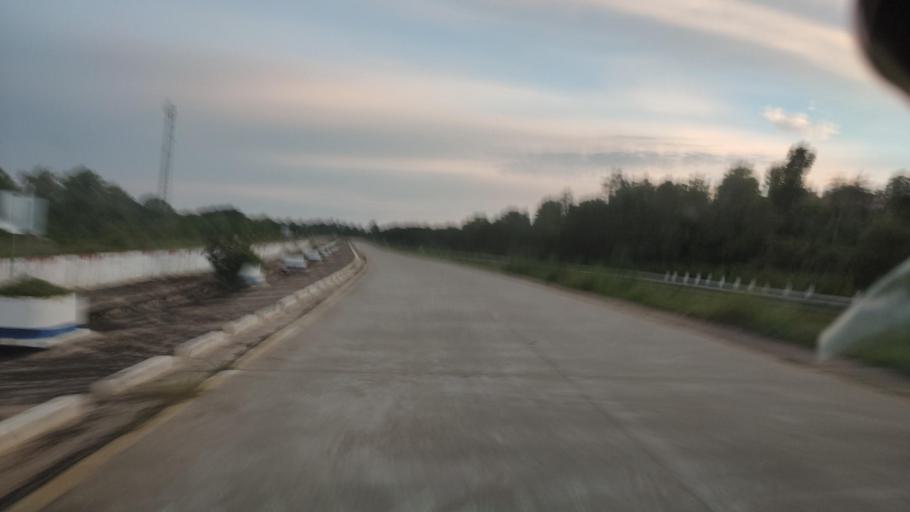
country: MM
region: Mandalay
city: Yamethin
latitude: 20.2221
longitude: 95.9034
